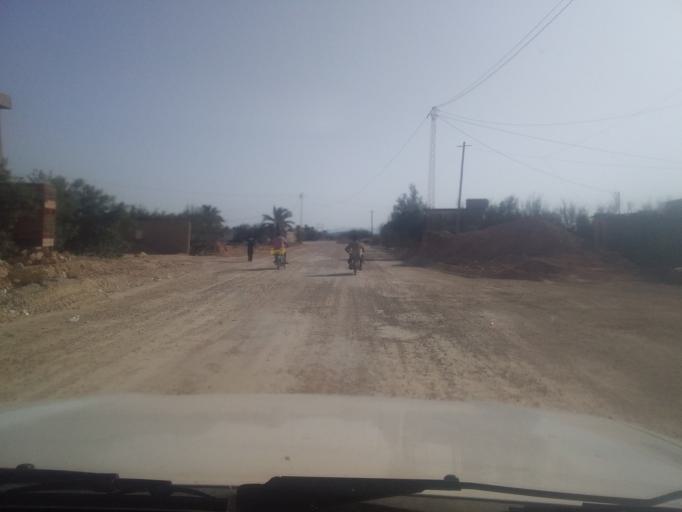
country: TN
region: Qabis
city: Matmata
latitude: 33.6043
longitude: 10.2781
